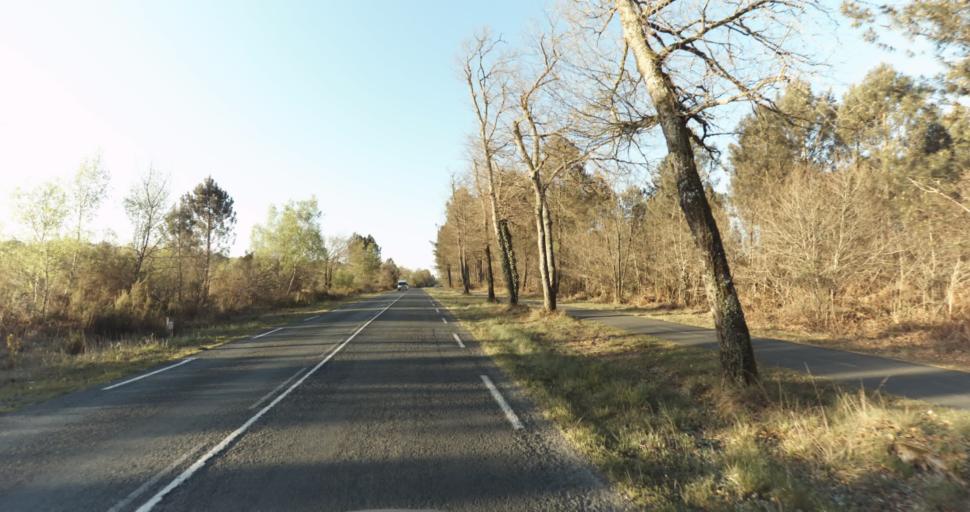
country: FR
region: Aquitaine
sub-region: Departement de la Gironde
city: Martignas-sur-Jalle
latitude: 44.8246
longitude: -0.7784
